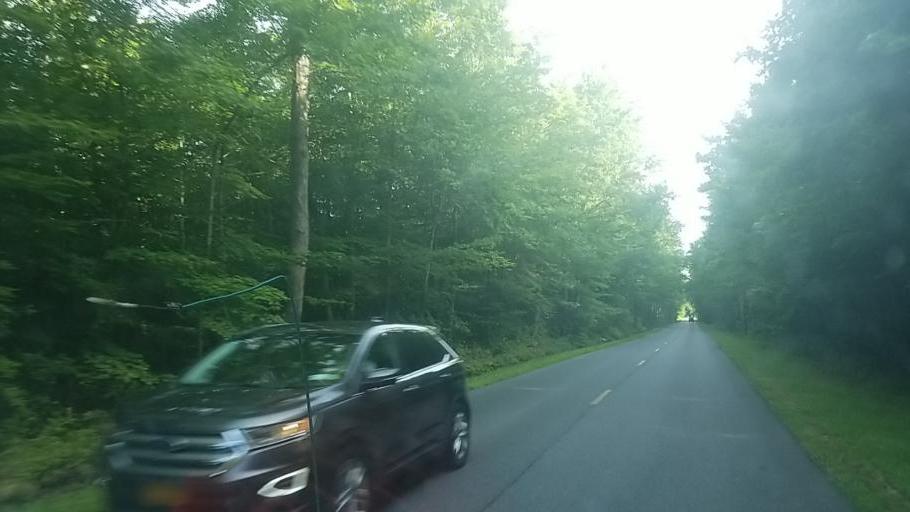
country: US
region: Maryland
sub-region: Worcester County
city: West Ocean City
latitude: 38.3351
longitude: -75.1560
